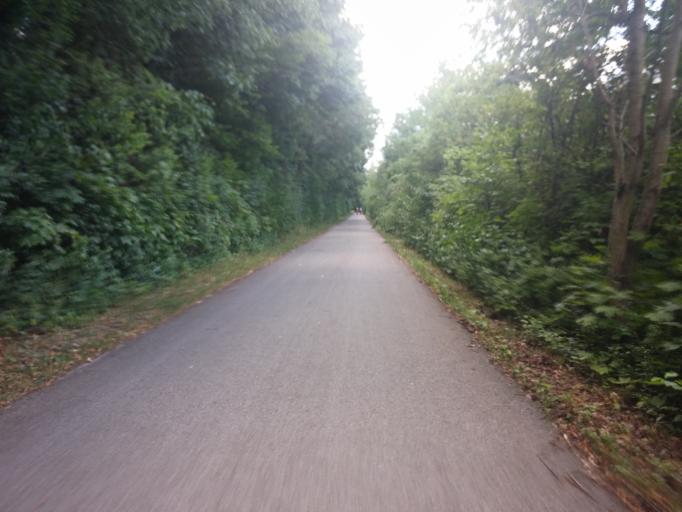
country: DE
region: Bavaria
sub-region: Upper Bavaria
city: Aschheim
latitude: 48.1459
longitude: 11.6894
